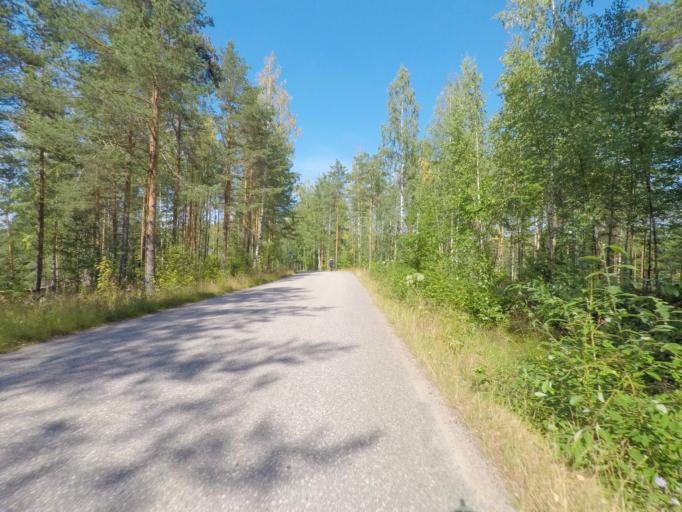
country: FI
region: Southern Savonia
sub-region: Mikkeli
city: Puumala
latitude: 61.4188
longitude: 28.0931
